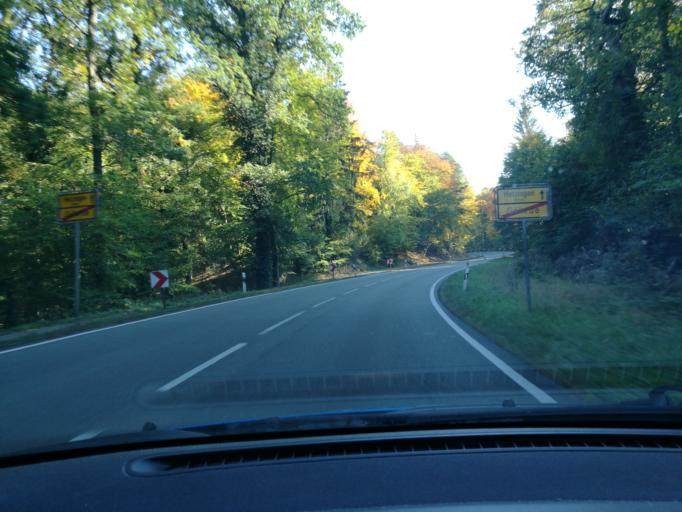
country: DE
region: Lower Saxony
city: Gohrde
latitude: 53.1373
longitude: 10.8833
